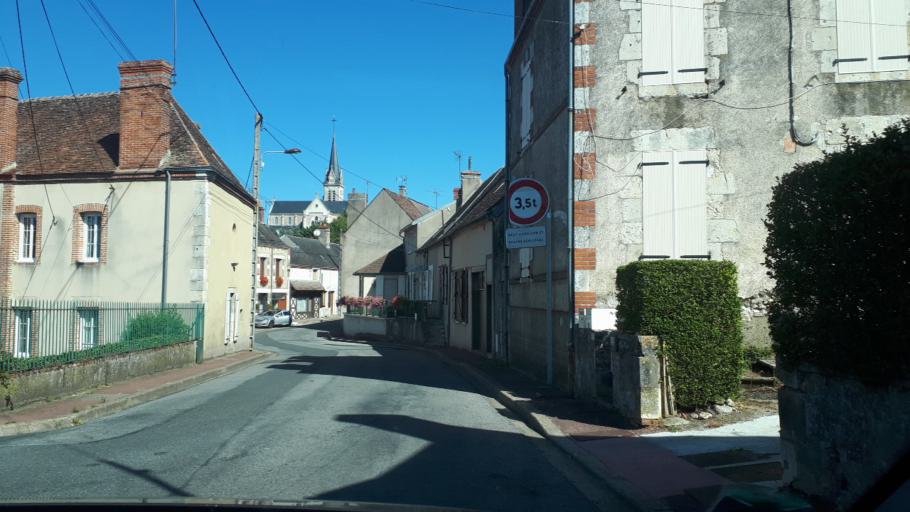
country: FR
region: Centre
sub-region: Departement du Loiret
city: Autry-le-Chatel
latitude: 47.5957
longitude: 2.6033
